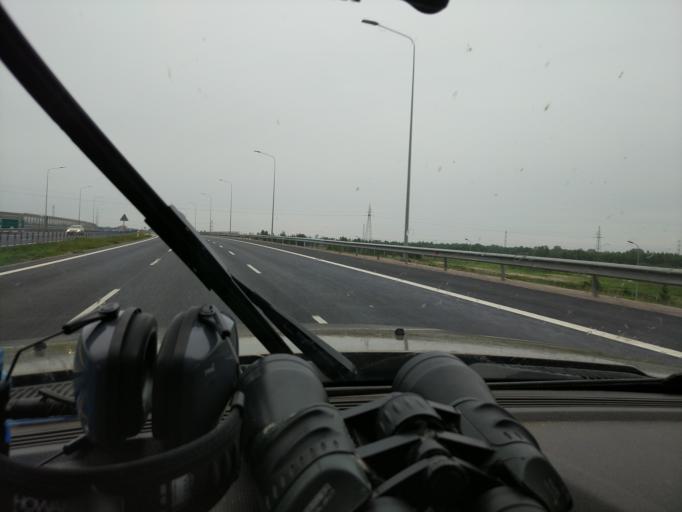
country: PL
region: Masovian Voivodeship
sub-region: Powiat wolominski
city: Radzymin
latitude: 52.3965
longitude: 21.2008
